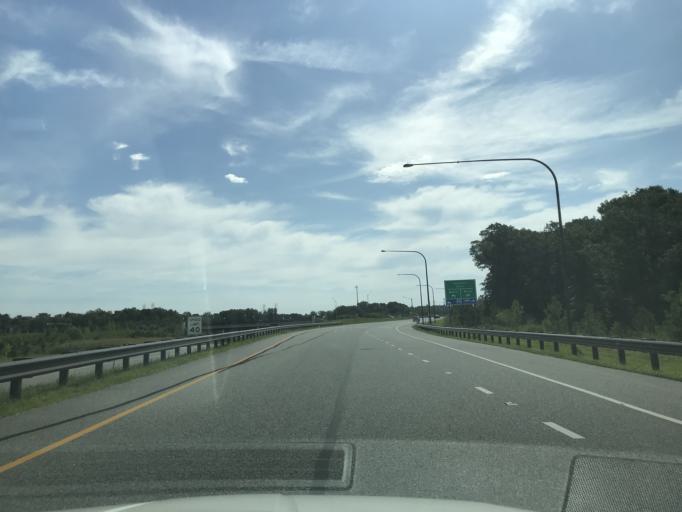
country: US
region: Maryland
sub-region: Prince George's County
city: West Laurel
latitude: 39.0671
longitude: -76.8926
